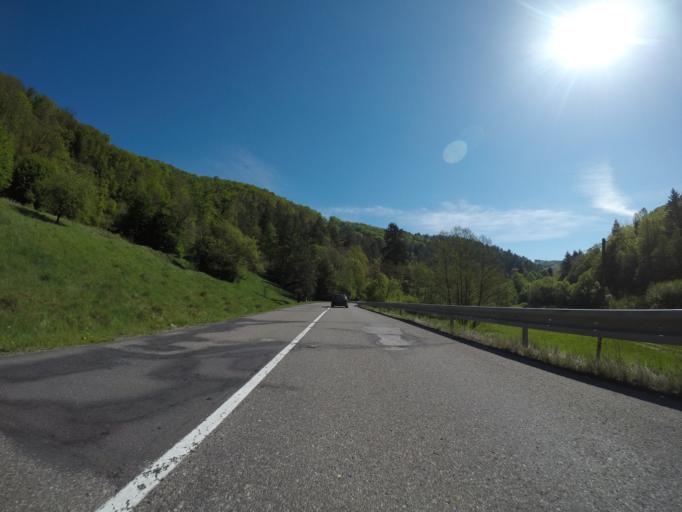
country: SK
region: Banskobystricky
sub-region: Okres Banska Bystrica
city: Banska Stiavnica
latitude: 48.5095
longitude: 18.9826
